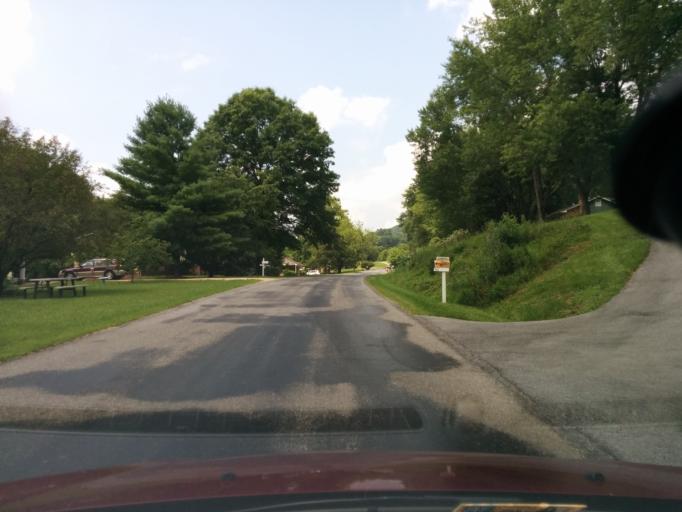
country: US
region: Virginia
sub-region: Rockbridge County
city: East Lexington
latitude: 37.8223
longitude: -79.3999
